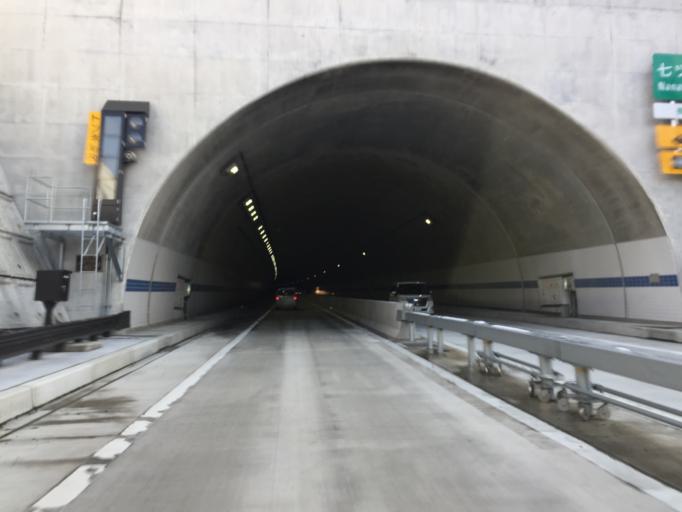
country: JP
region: Fukushima
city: Hobaramachi
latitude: 37.7547
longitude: 140.6220
